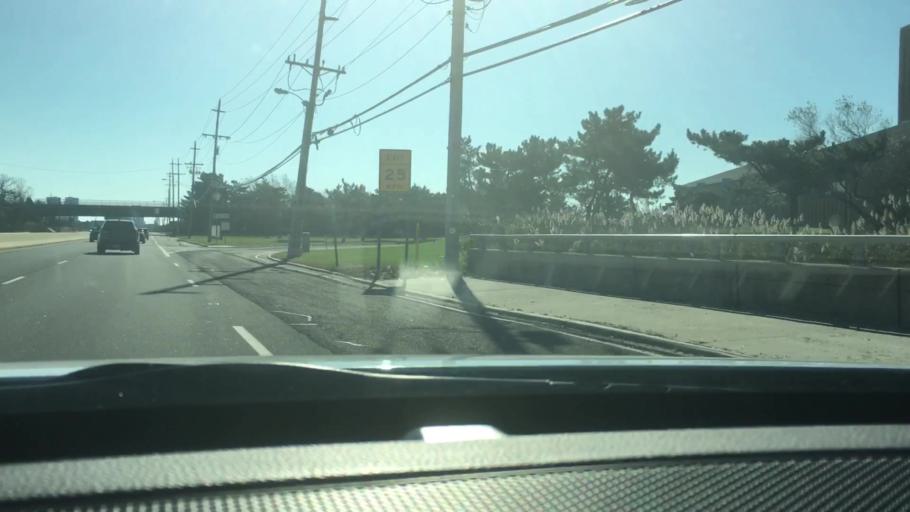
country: US
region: New Jersey
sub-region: Atlantic County
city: Ventnor City
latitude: 39.3693
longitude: -74.4755
